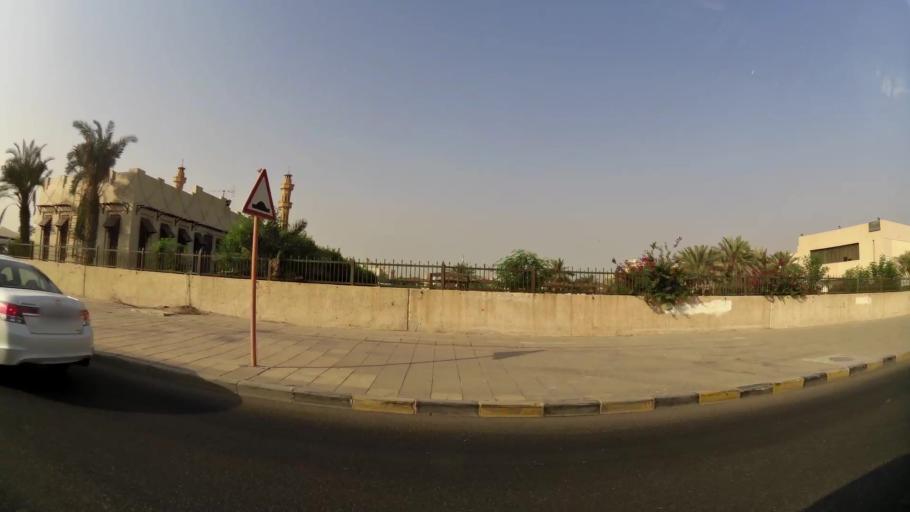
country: KW
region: Muhafazat Hawalli
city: Salwa
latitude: 29.2788
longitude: 48.0710
